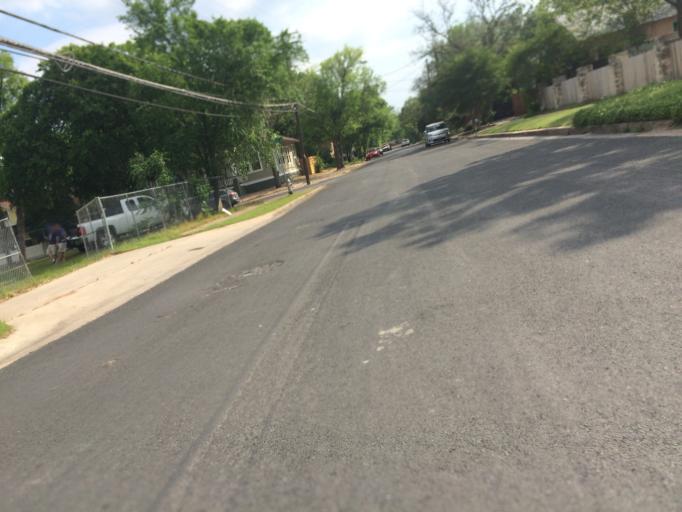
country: US
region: Texas
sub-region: Travis County
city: Austin
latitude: 30.3011
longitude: -97.7415
